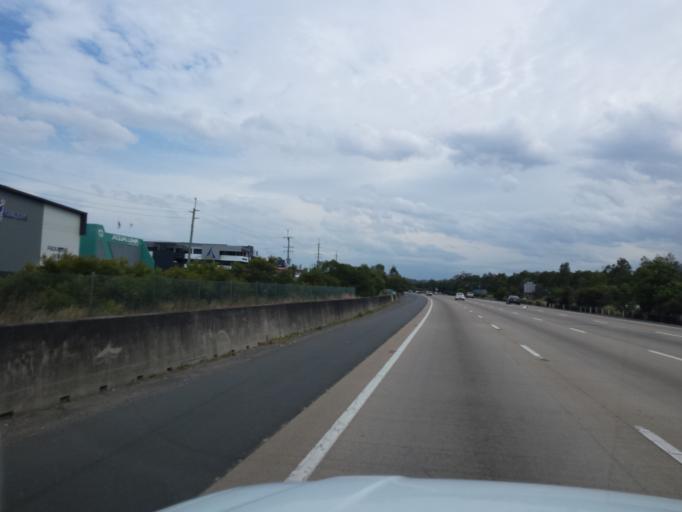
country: AU
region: Queensland
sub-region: Gold Coast
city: Oxenford
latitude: -27.8944
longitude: 153.3146
